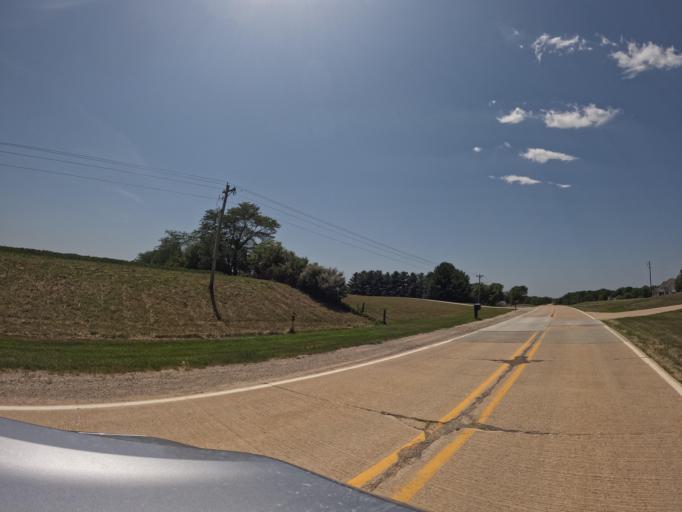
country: US
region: Iowa
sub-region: Henry County
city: Mount Pleasant
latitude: 40.9805
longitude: -91.6025
